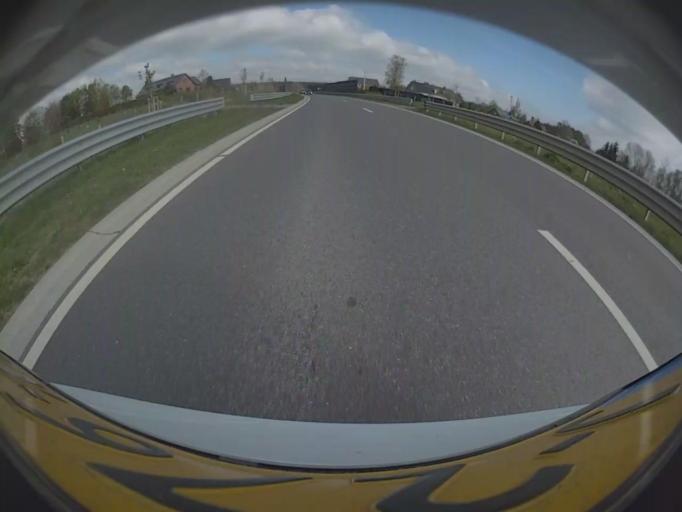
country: BE
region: Wallonia
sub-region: Province du Luxembourg
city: Marche-en-Famenne
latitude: 50.2289
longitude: 5.3142
